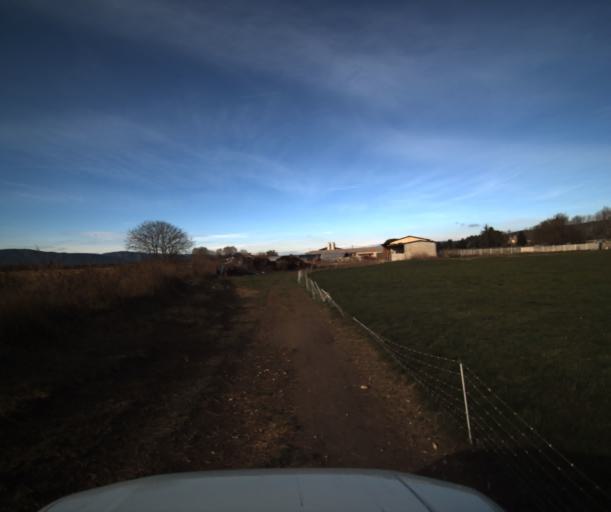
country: FR
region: Provence-Alpes-Cote d'Azur
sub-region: Departement du Vaucluse
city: Pertuis
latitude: 43.6870
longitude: 5.4734
